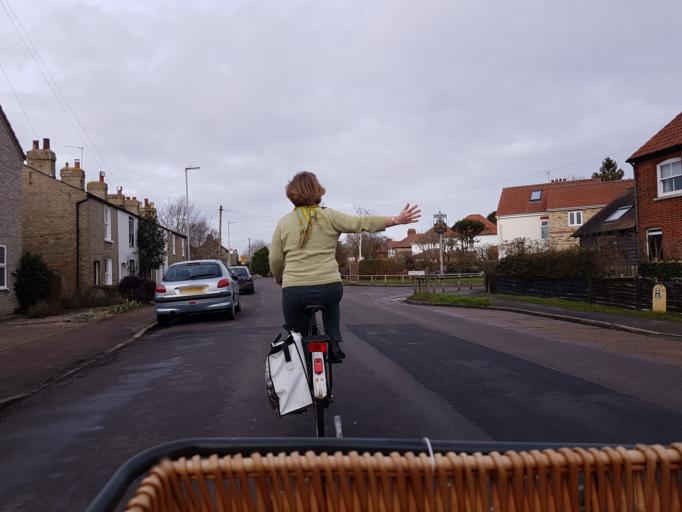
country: GB
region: England
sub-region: Cambridgeshire
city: Girton
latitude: 52.2378
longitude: 0.0846
